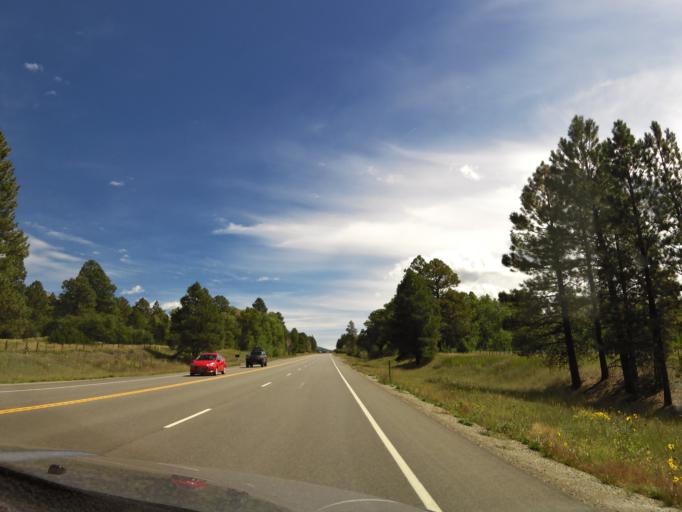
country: US
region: Colorado
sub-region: Montezuma County
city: Mancos
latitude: 37.3235
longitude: -108.1580
